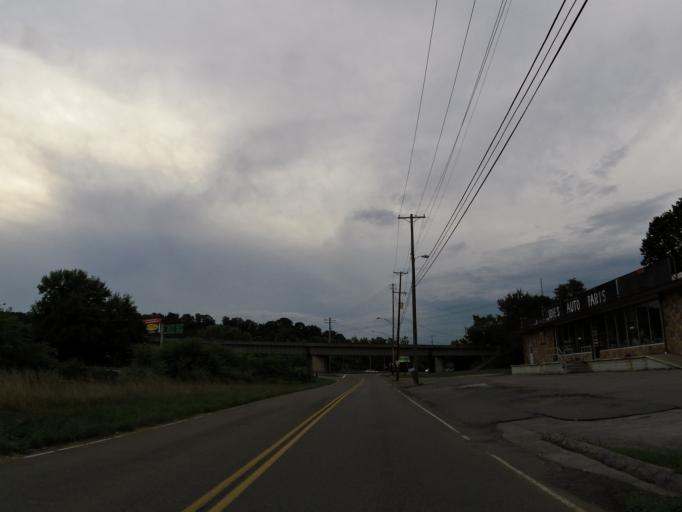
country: US
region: Tennessee
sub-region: Knox County
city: Knoxville
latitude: 36.0158
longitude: -83.9218
